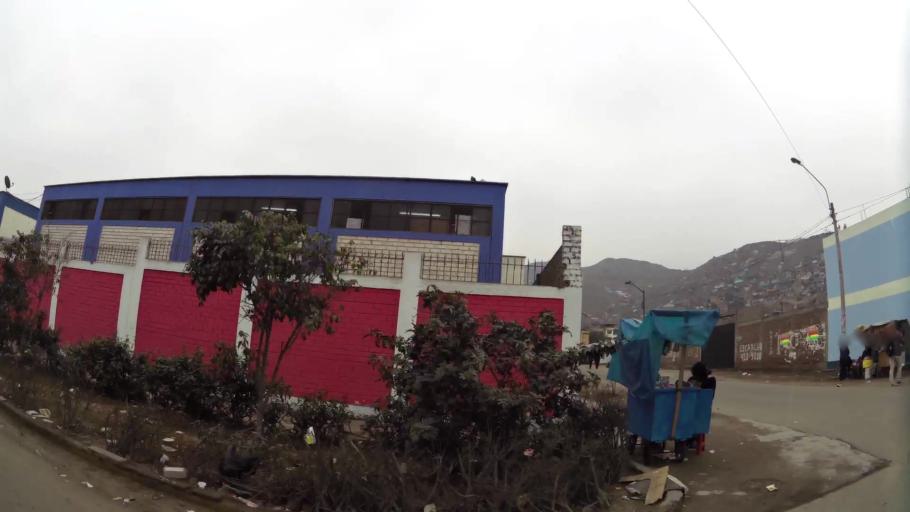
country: PE
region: Lima
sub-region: Lima
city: Independencia
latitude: -11.9528
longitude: -76.9921
